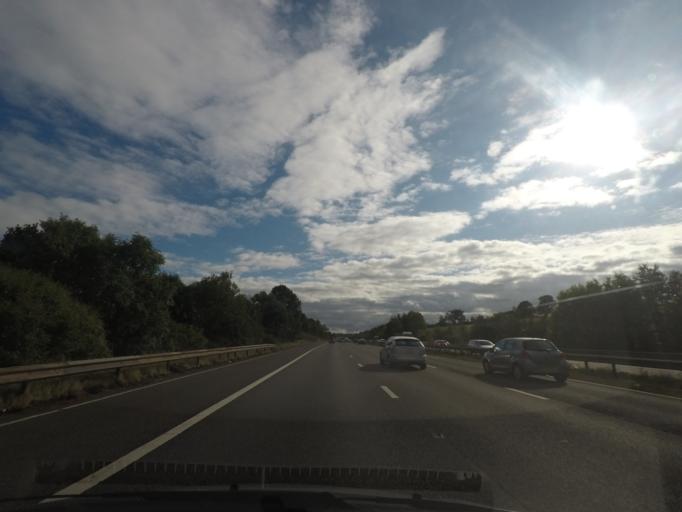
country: GB
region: England
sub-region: Leicestershire
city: Shepshed
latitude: 52.7428
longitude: -1.2780
